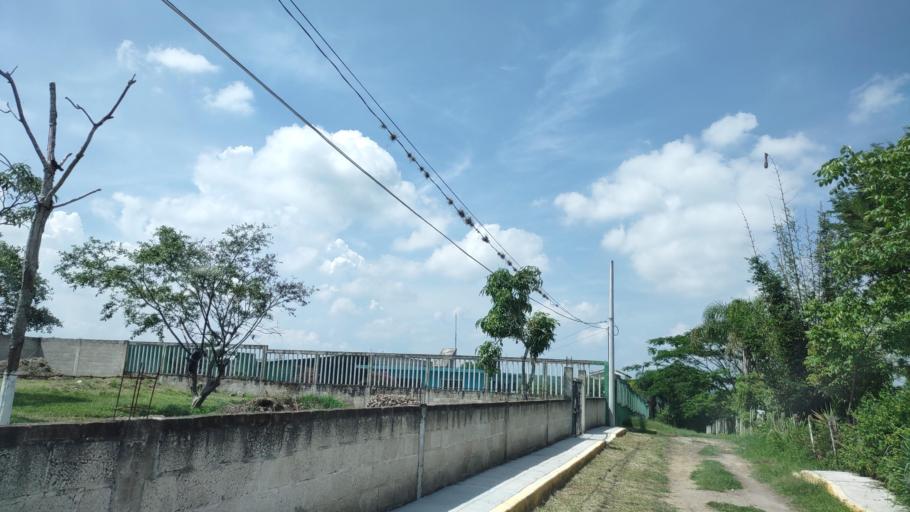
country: MX
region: Veracruz
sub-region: Emiliano Zapata
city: Dos Rios
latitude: 19.4291
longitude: -96.8076
